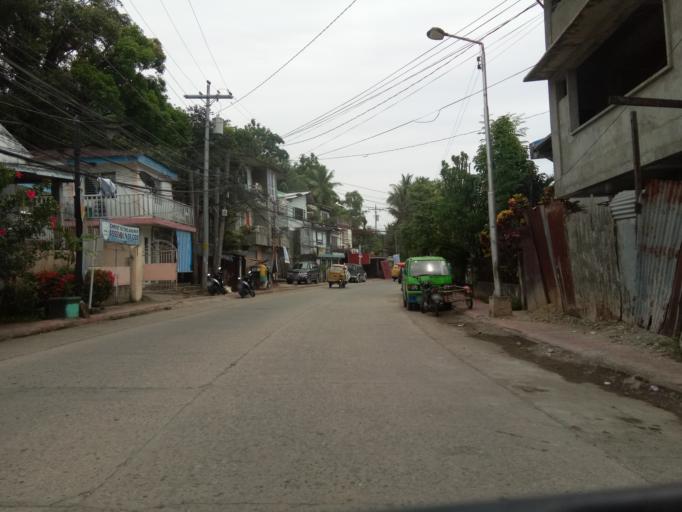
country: PH
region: Caraga
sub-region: Province of Surigao del Norte
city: Surigao
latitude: 9.7850
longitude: 125.4919
